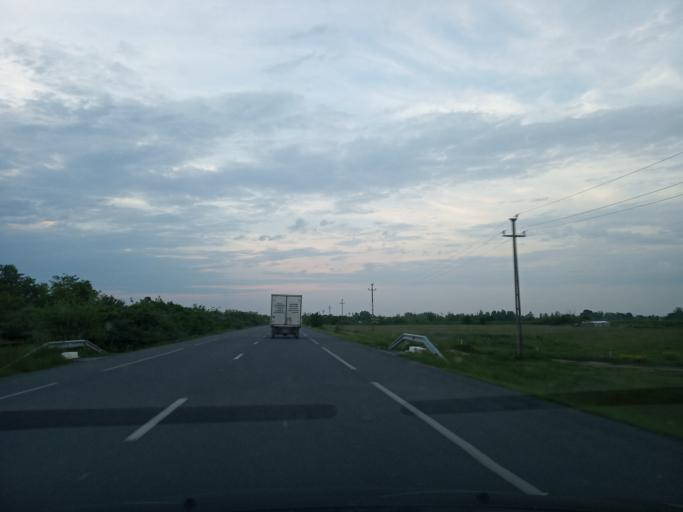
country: RO
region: Timis
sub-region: Oras Deta
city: Deta
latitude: 45.3868
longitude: 21.2320
